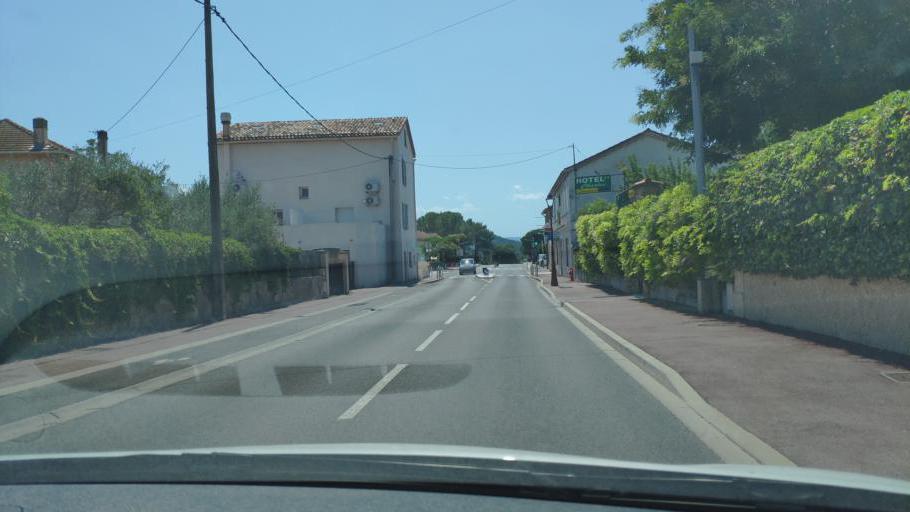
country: FR
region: Provence-Alpes-Cote d'Azur
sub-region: Departement du Var
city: Les Arcs
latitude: 43.4560
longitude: 6.4801
